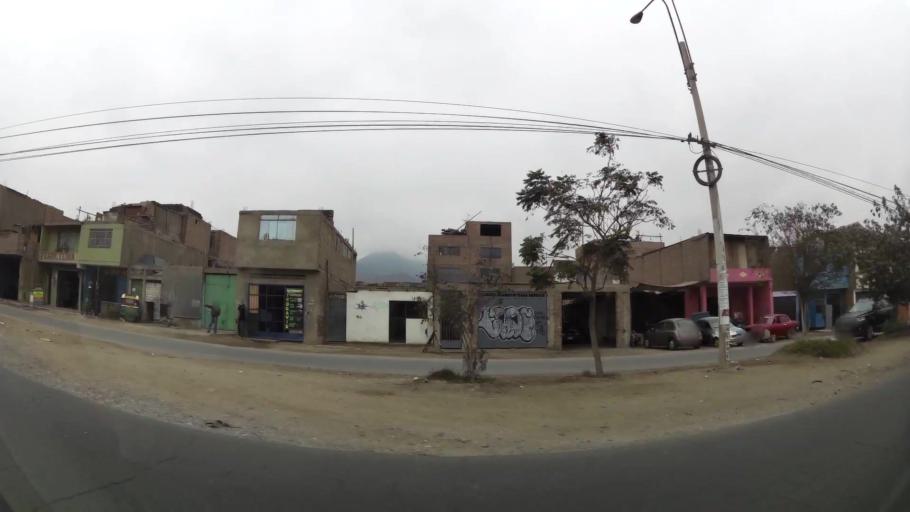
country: PE
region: Lima
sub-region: Lima
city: Independencia
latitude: -11.9522
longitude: -77.0596
